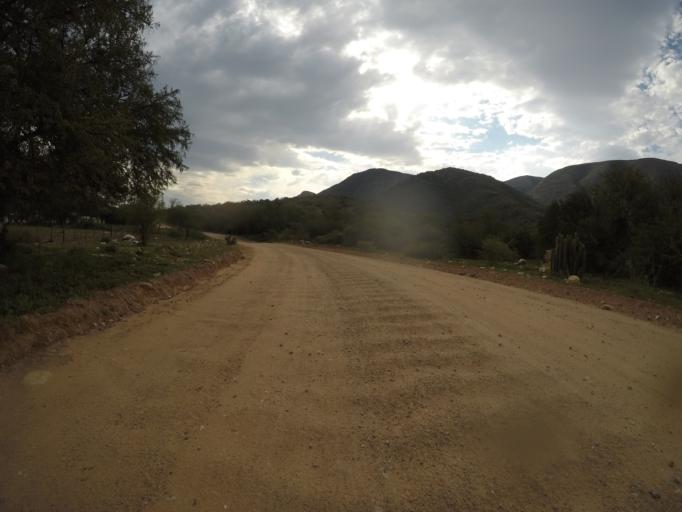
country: ZA
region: Eastern Cape
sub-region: Cacadu District Municipality
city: Kareedouw
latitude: -33.5832
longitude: 24.1655
